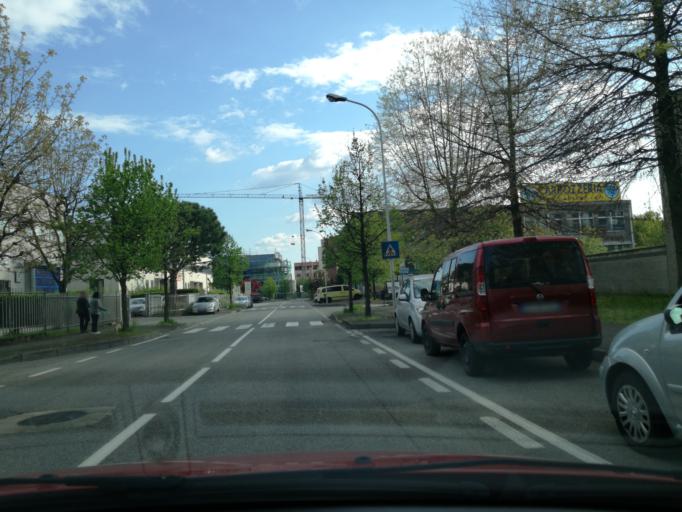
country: IT
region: Lombardy
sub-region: Provincia di Monza e Brianza
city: Seregno
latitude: 45.6536
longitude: 9.2221
